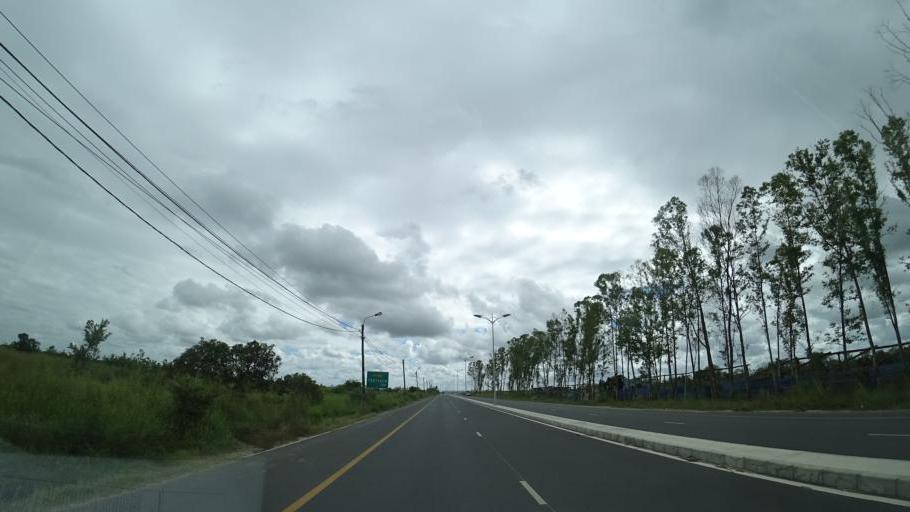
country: MZ
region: Sofala
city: Dondo
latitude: -19.6843
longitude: 34.7782
